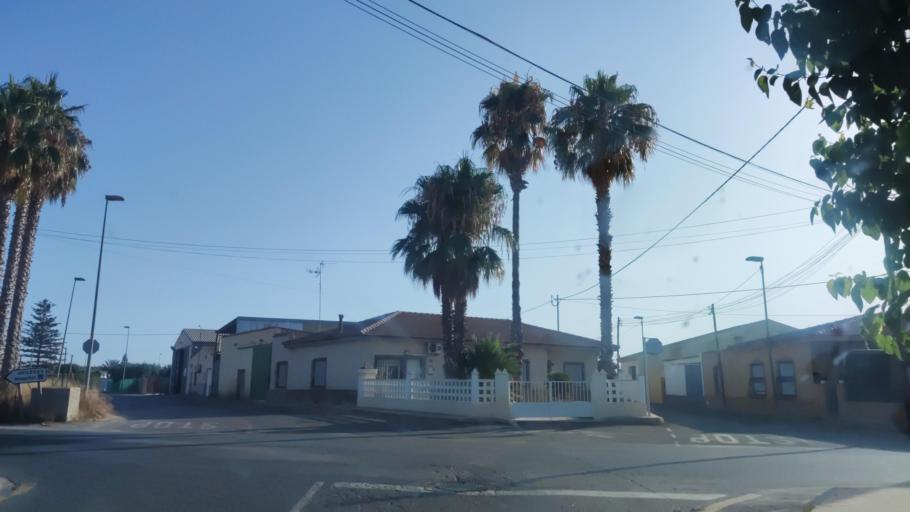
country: ES
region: Murcia
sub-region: Murcia
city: San Javier
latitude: 37.8079
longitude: -0.8573
